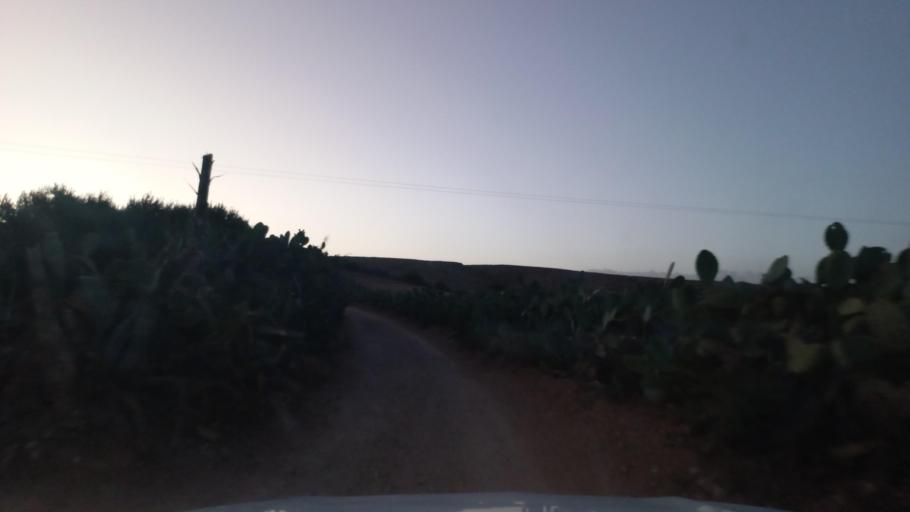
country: TN
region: Al Qasrayn
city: Sbiba
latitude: 35.3782
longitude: 9.0161
